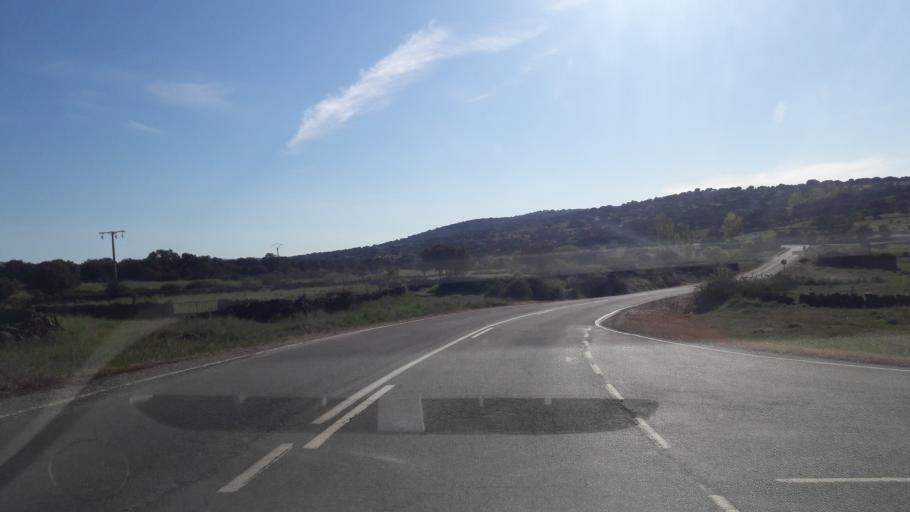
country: ES
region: Castille and Leon
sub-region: Provincia de Salamanca
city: Puente del Congosto
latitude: 40.5238
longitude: -5.4974
